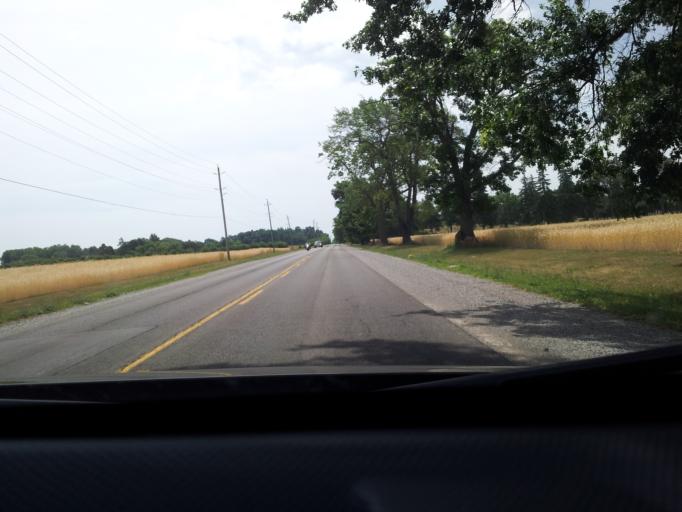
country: CA
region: Ontario
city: Norfolk County
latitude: 42.7972
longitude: -80.2429
